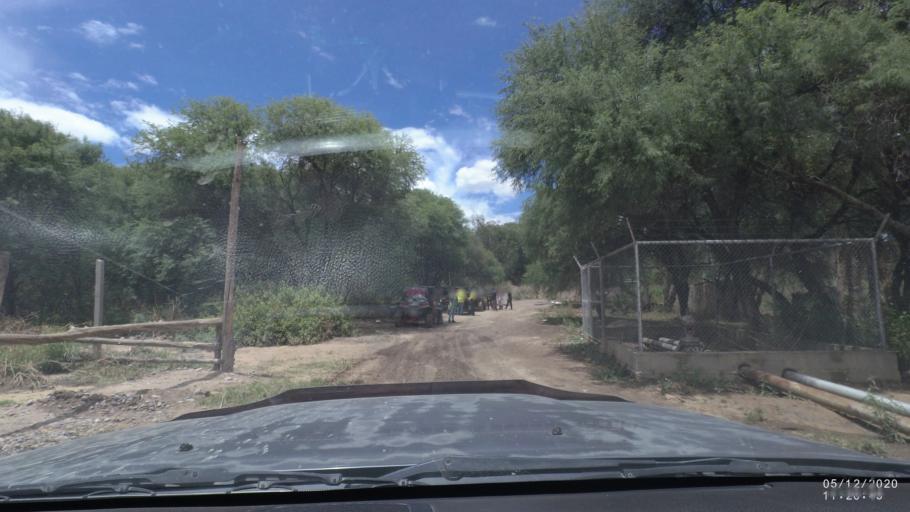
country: BO
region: Cochabamba
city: Sipe Sipe
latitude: -17.5526
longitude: -66.3382
